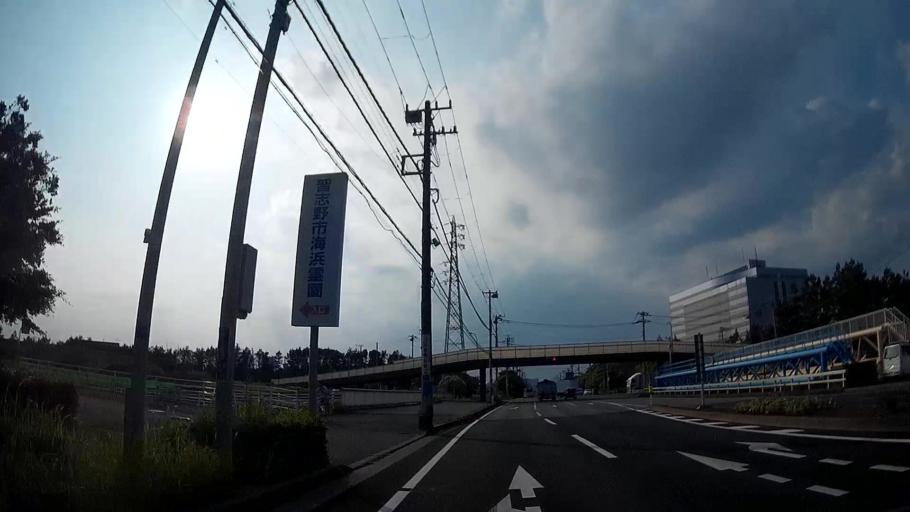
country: JP
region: Chiba
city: Funabashi
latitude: 35.6618
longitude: 140.0118
